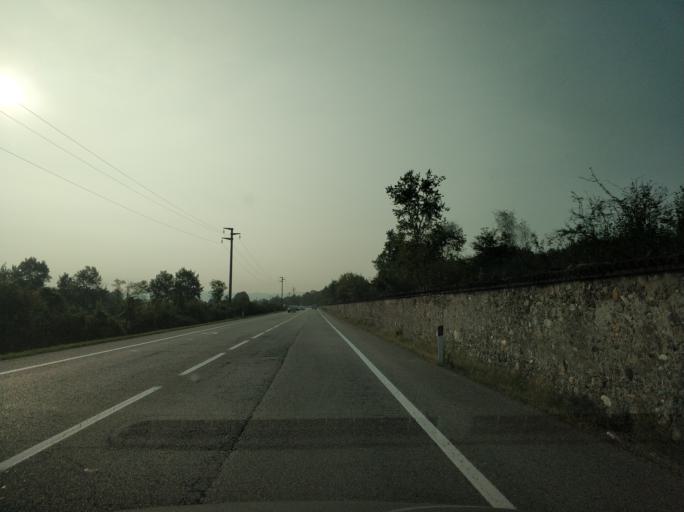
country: IT
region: Piedmont
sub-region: Provincia di Torino
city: Druento
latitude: 45.1658
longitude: 7.5964
